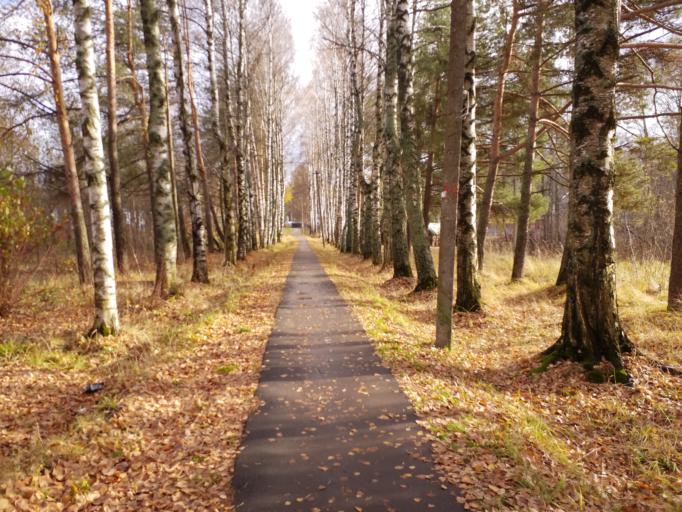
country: RU
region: Moskovskaya
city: Ashukino
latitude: 56.1631
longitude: 37.9426
